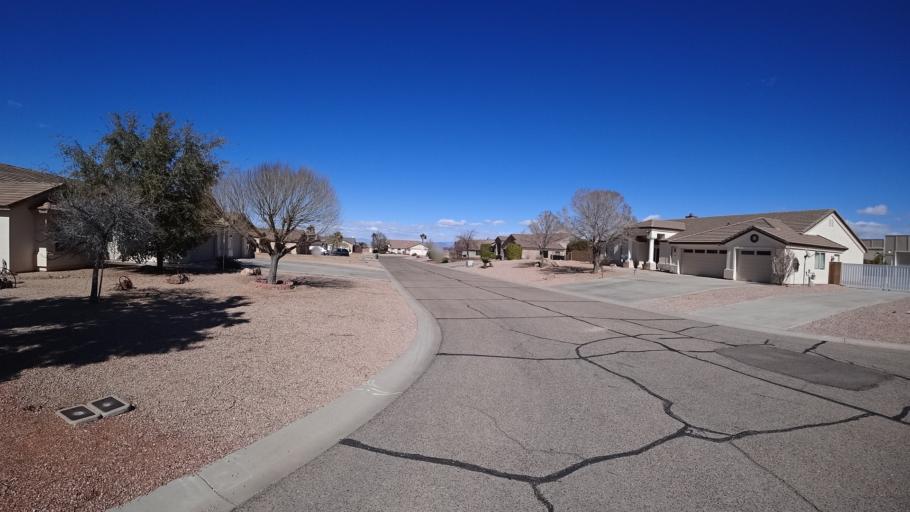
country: US
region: Arizona
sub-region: Mohave County
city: New Kingman-Butler
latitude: 35.2087
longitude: -113.9728
